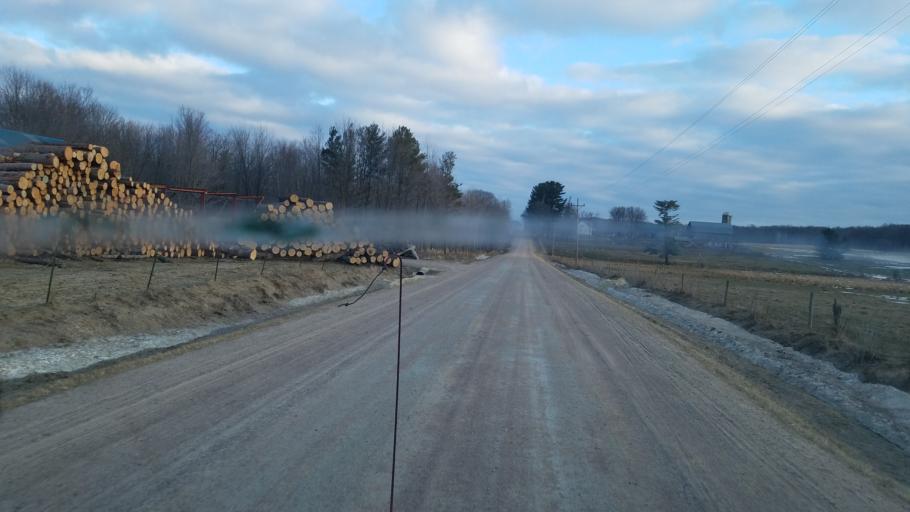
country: US
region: Wisconsin
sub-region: Clark County
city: Loyal
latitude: 44.6197
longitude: -90.4360
